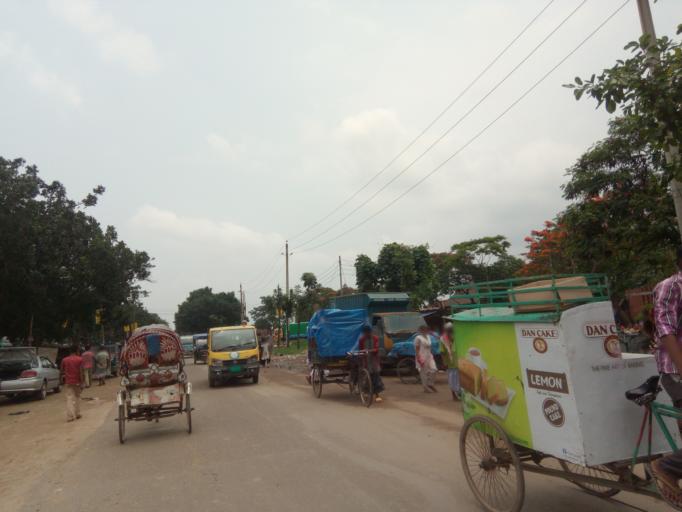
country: BD
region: Dhaka
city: Azimpur
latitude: 23.7522
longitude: 90.3577
